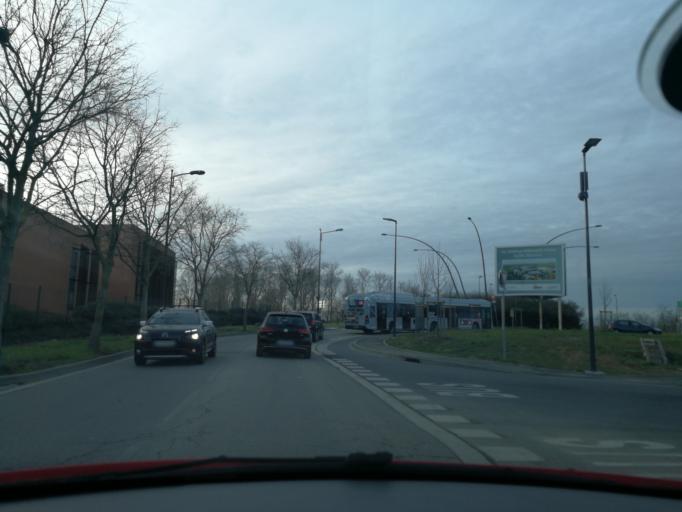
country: FR
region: Midi-Pyrenees
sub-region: Departement de la Haute-Garonne
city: Blagnac
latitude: 43.6266
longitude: 1.4112
